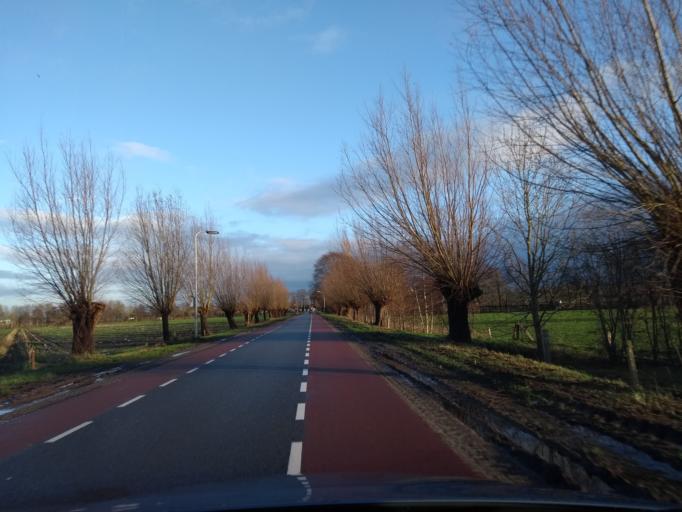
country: NL
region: Overijssel
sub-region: Gemeente Wierden
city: Wierden
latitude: 52.3994
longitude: 6.5809
